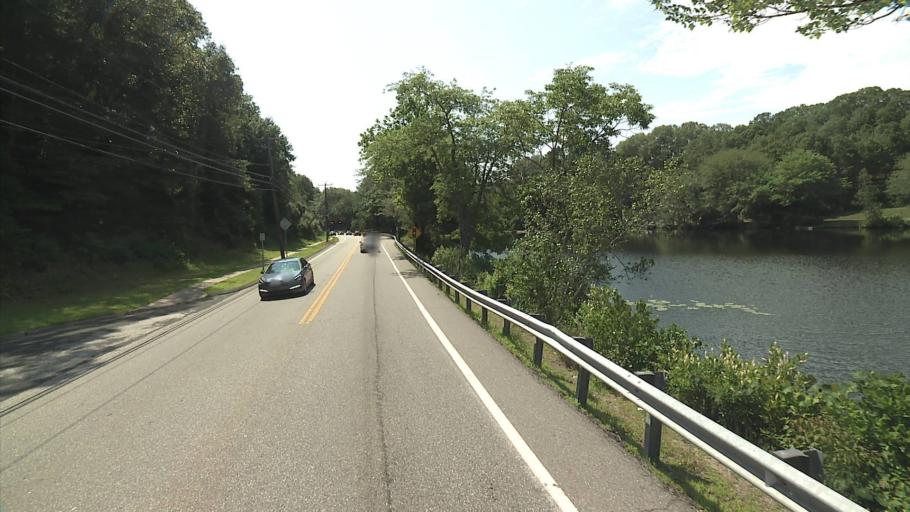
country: US
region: Connecticut
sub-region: New London County
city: Niantic
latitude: 41.3372
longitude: -72.2073
